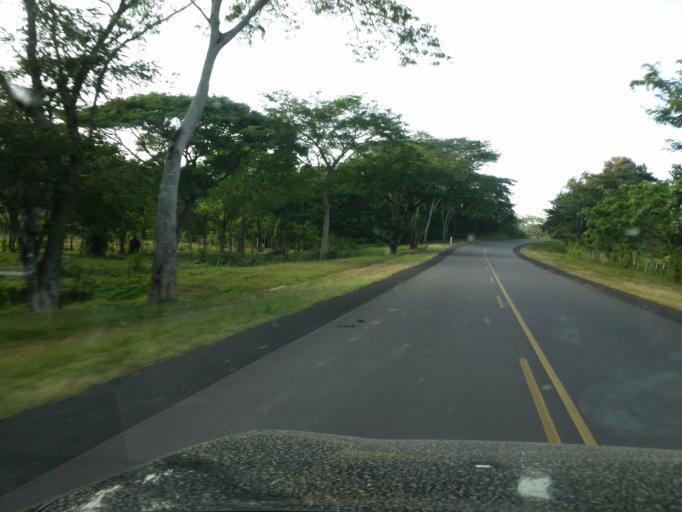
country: NI
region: Rio San Juan
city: San Miguelito
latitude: 11.3679
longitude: -84.7717
